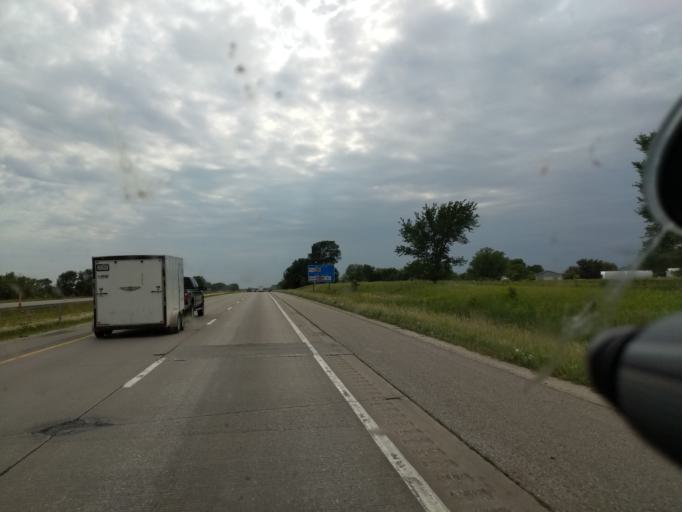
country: US
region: Iowa
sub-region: Dallas County
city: Waukee
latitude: 41.5794
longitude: -93.8341
